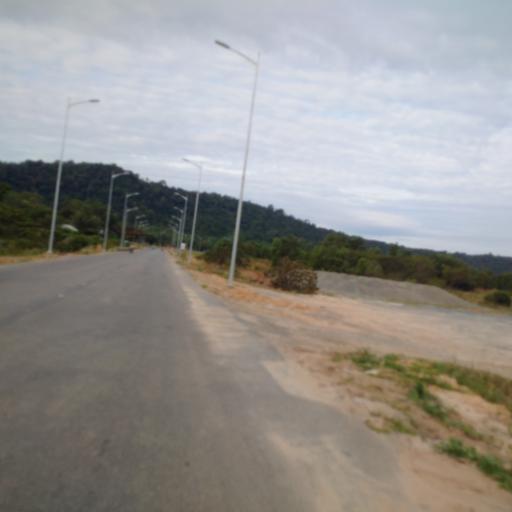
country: VN
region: Kien Giang
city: Duong GJong
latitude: 10.1597
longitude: 104.0042
